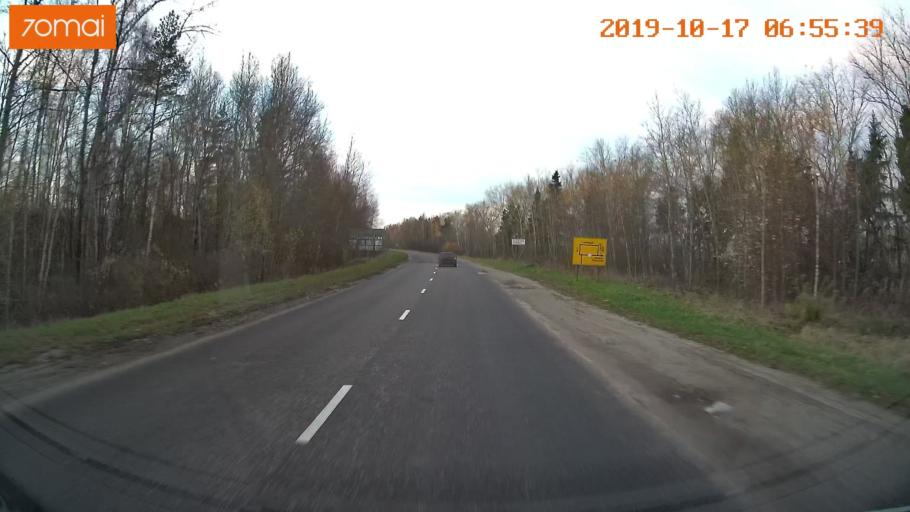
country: RU
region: Vladimir
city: Suzdal'
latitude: 56.4544
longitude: 40.4548
